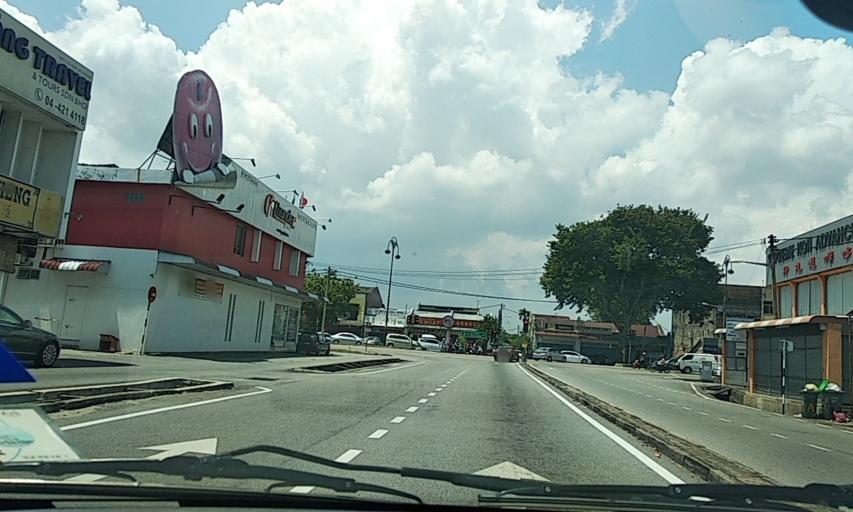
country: MY
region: Kedah
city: Sungai Petani
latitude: 5.6339
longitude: 100.4827
